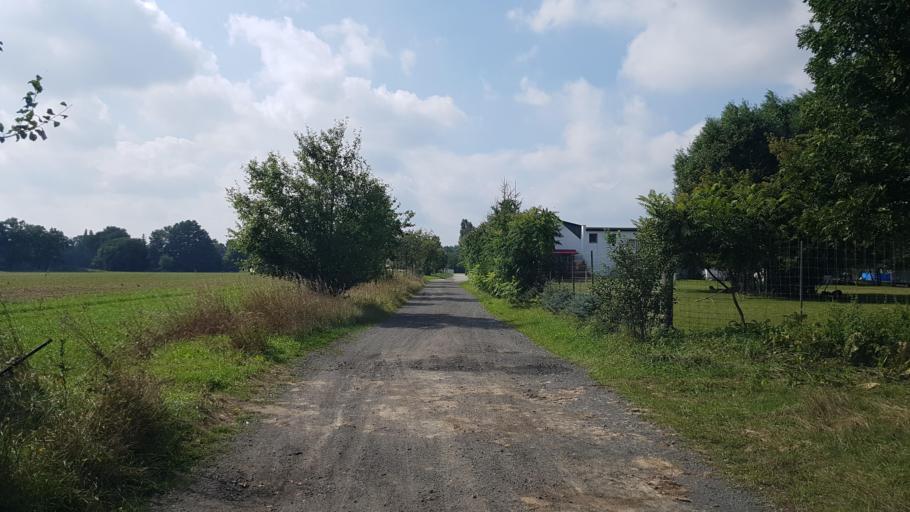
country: DE
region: Brandenburg
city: Luckau
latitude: 51.8250
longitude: 13.6581
